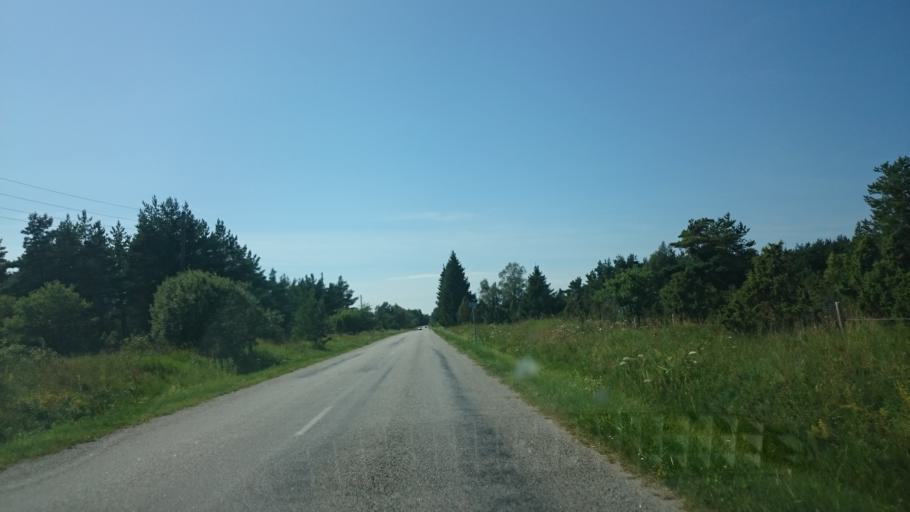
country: EE
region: Saare
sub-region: Orissaare vald
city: Orissaare
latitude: 58.5694
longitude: 22.7562
